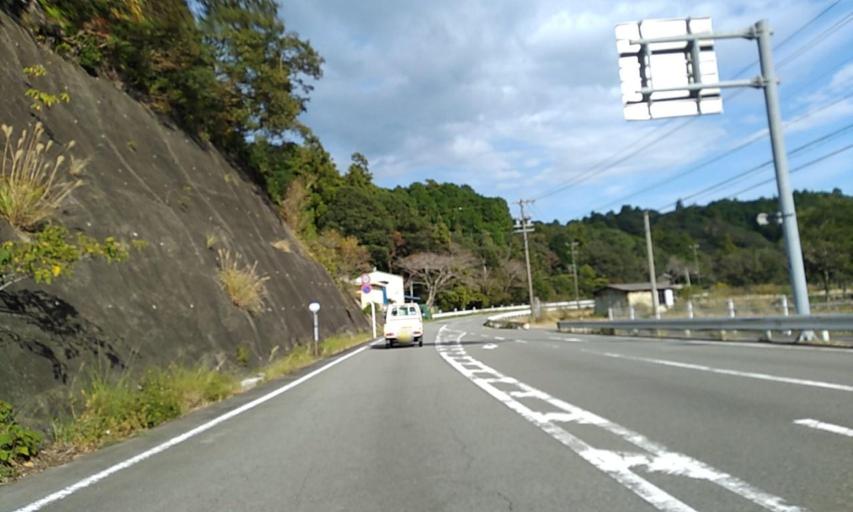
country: JP
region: Mie
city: Ise
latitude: 34.2978
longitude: 136.5903
